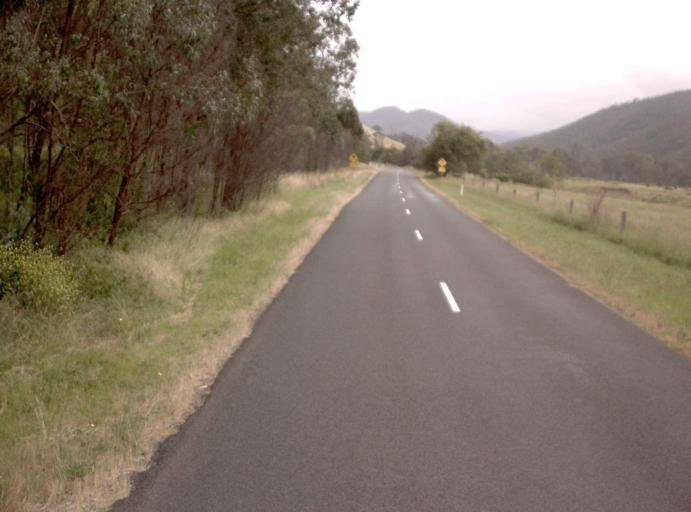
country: AU
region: Victoria
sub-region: Wellington
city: Heyfield
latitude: -37.7767
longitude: 146.6667
